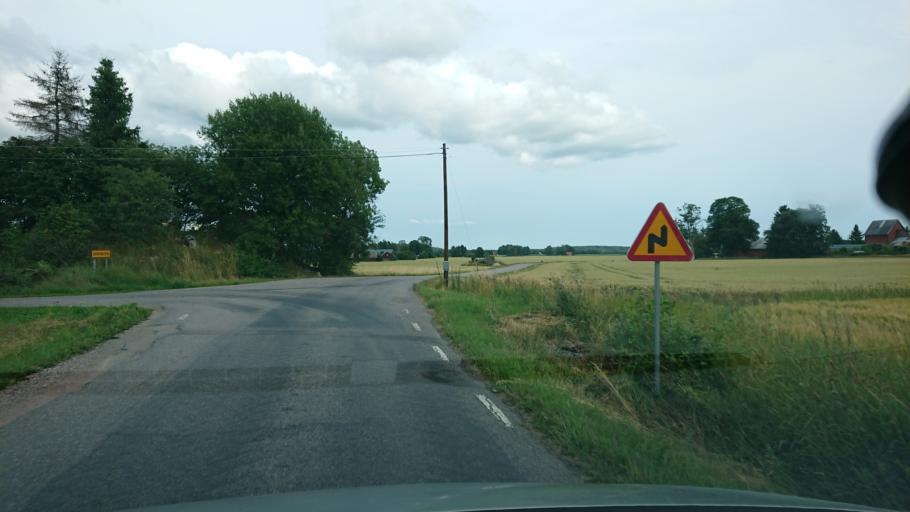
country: SE
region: Uppsala
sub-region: Osthammars Kommun
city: Bjorklinge
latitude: 59.9903
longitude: 17.5286
